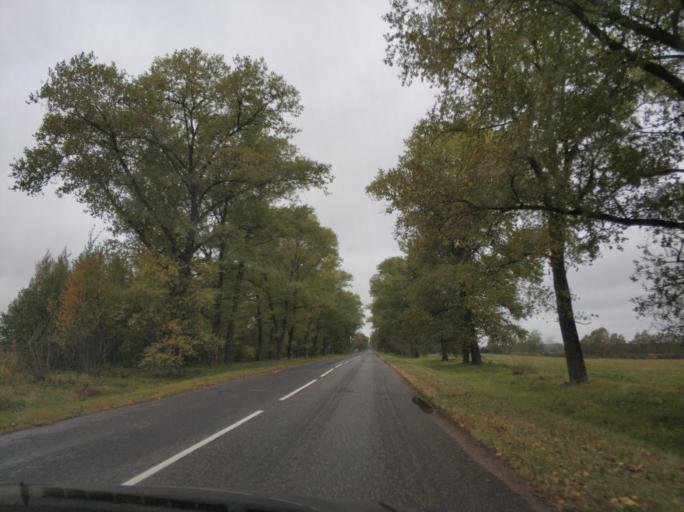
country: BY
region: Vitebsk
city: Polatsk
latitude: 55.4361
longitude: 28.9741
